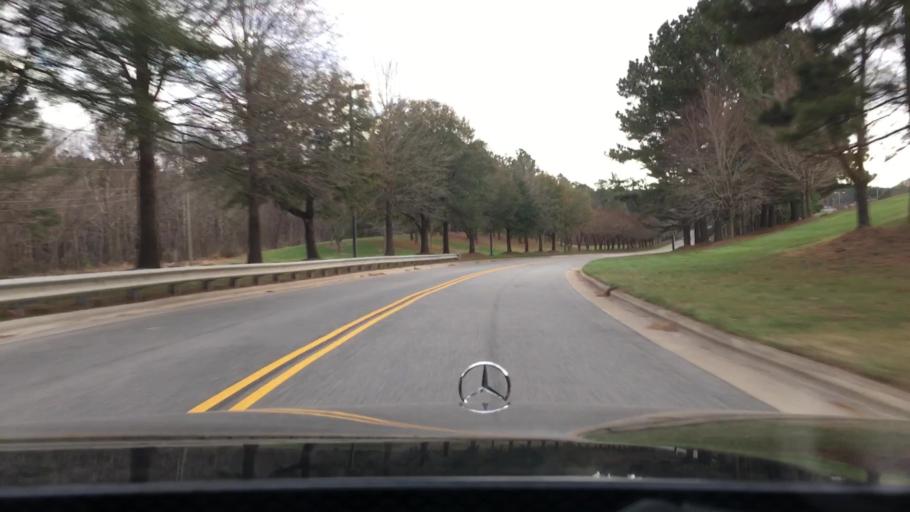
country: US
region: North Carolina
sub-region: Wake County
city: Morrisville
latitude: 35.8952
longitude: -78.7700
